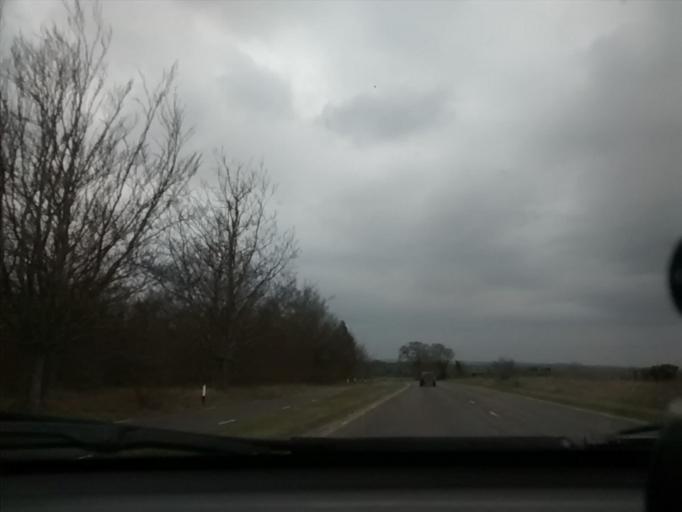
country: GB
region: England
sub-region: Cambridgeshire
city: Sawston
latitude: 52.1496
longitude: 0.1910
